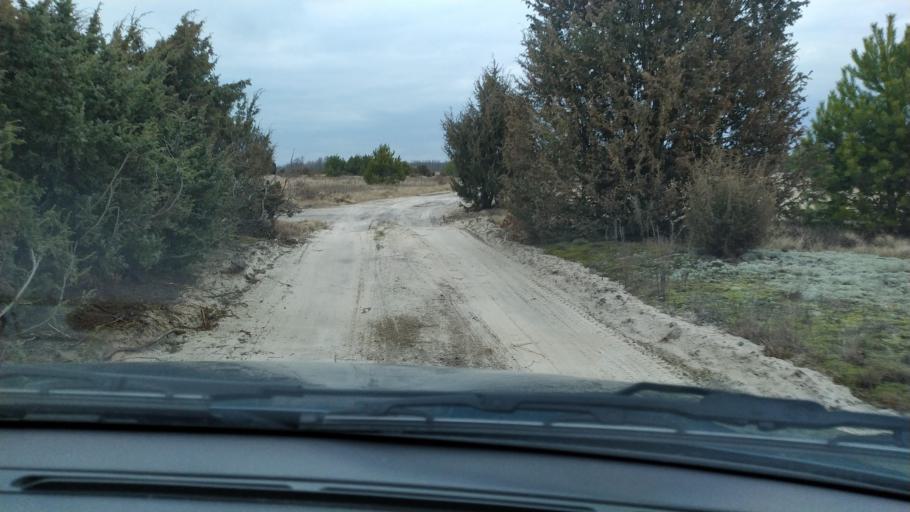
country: BY
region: Brest
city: Kamyanyets
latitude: 52.4221
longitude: 23.8379
